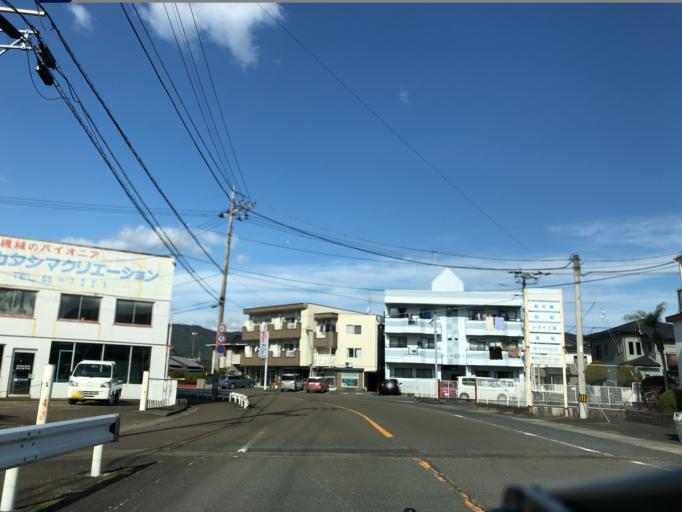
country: JP
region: Kochi
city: Sukumo
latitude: 32.9259
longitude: 132.7022
